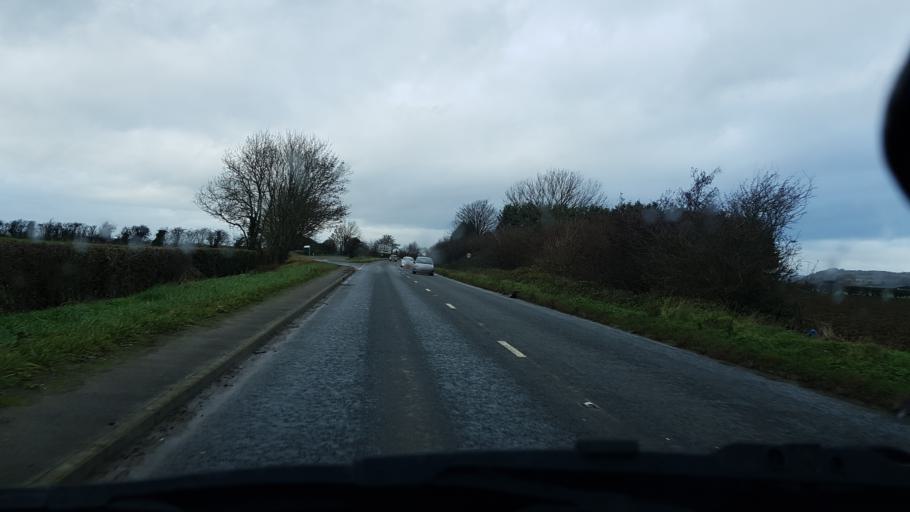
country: GB
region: England
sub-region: Gloucestershire
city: Gotherington
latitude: 51.9587
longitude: -2.0676
